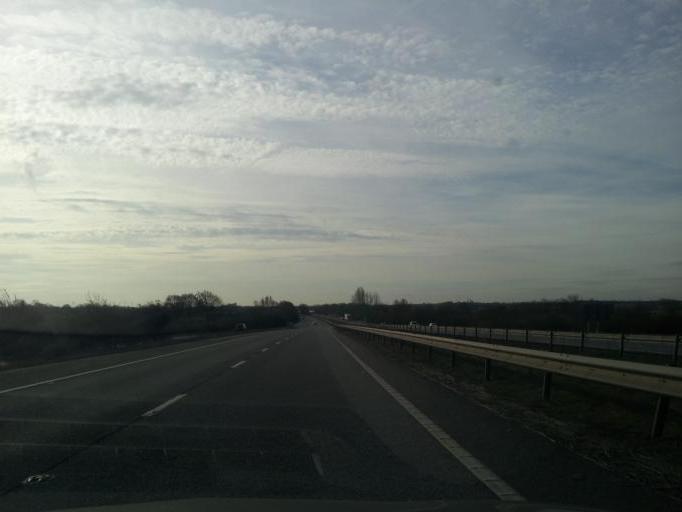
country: GB
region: England
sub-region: Cambridgeshire
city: Brampton
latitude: 52.3304
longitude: -0.2478
